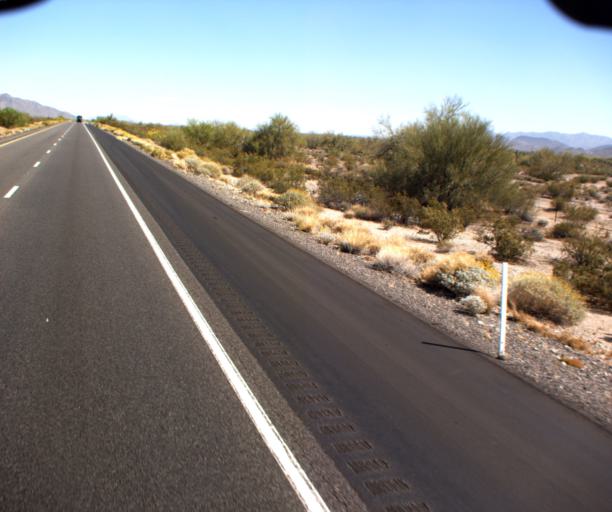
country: US
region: Arizona
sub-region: Maricopa County
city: Gila Bend
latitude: 32.8903
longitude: -112.4838
